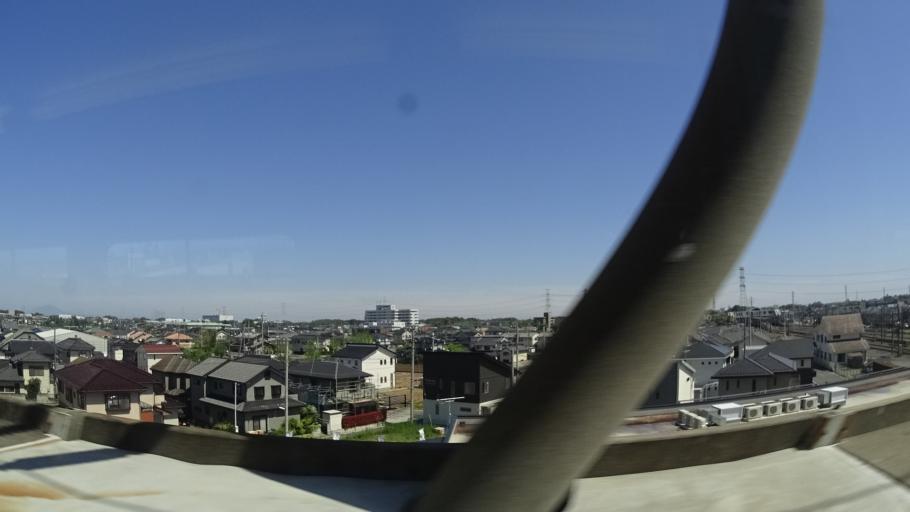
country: JP
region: Saitama
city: Kurihashi
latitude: 36.1173
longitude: 139.7104
